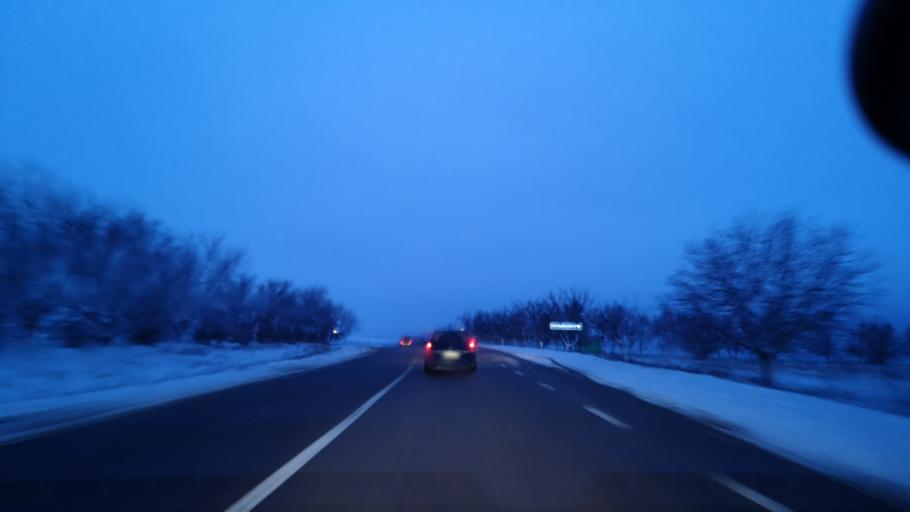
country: MD
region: Rezina
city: Saharna
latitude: 47.6269
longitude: 28.8350
